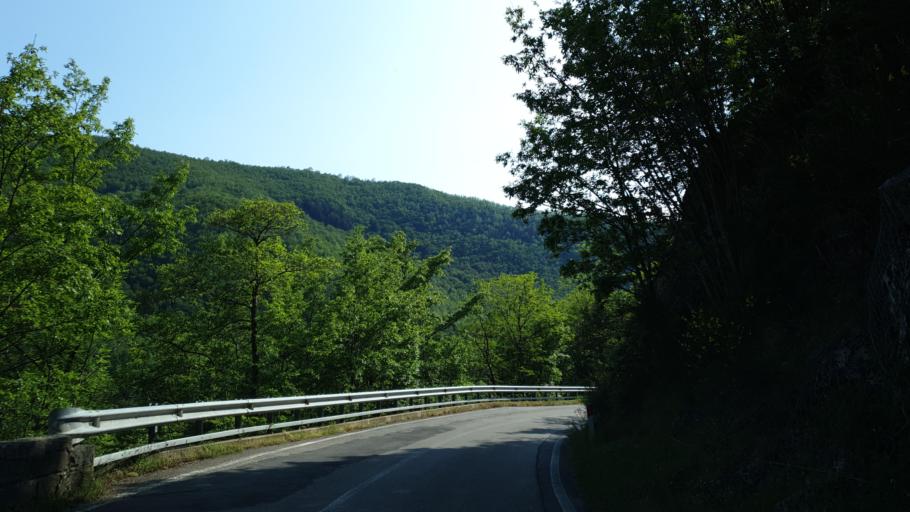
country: IT
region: Tuscany
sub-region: Province of Arezzo
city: Soci
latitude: 43.7713
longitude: 11.8643
